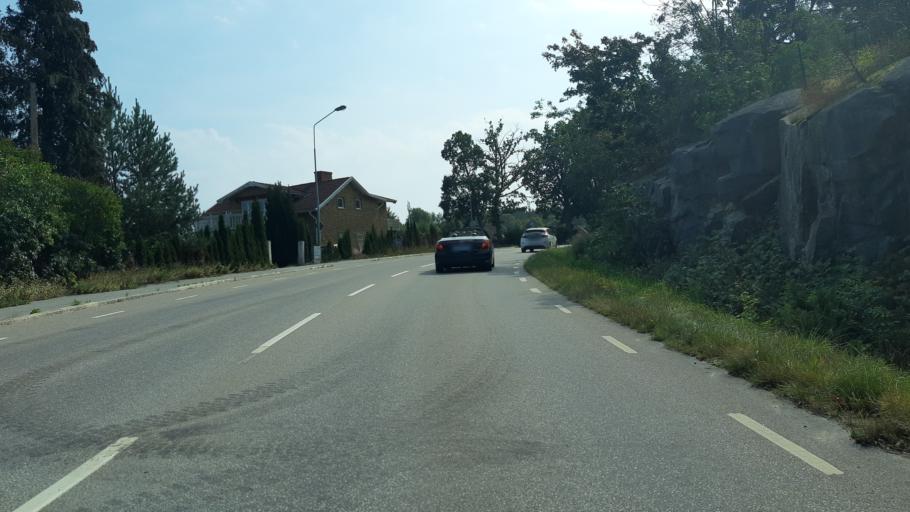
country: SE
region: Blekinge
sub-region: Karlskrona Kommun
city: Nattraby
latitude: 56.1949
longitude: 15.5353
